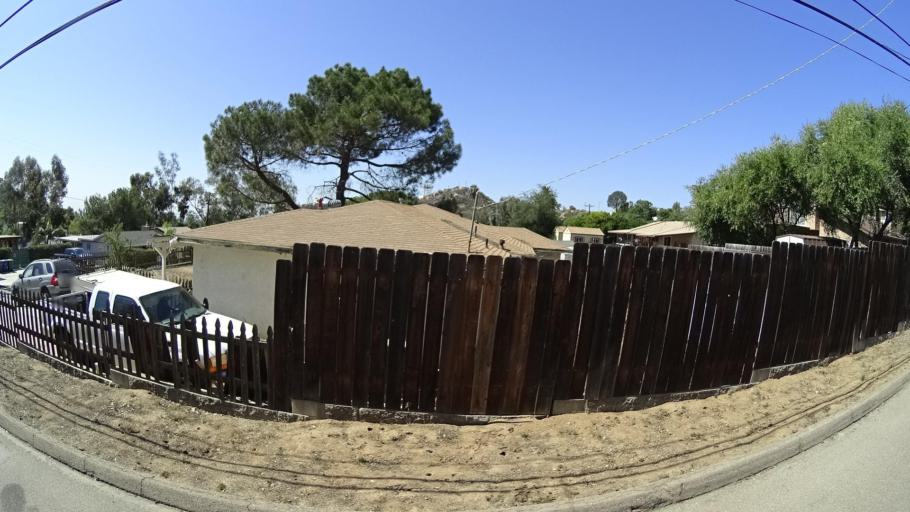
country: US
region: California
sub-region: San Diego County
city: Crest
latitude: 32.8051
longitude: -116.8691
